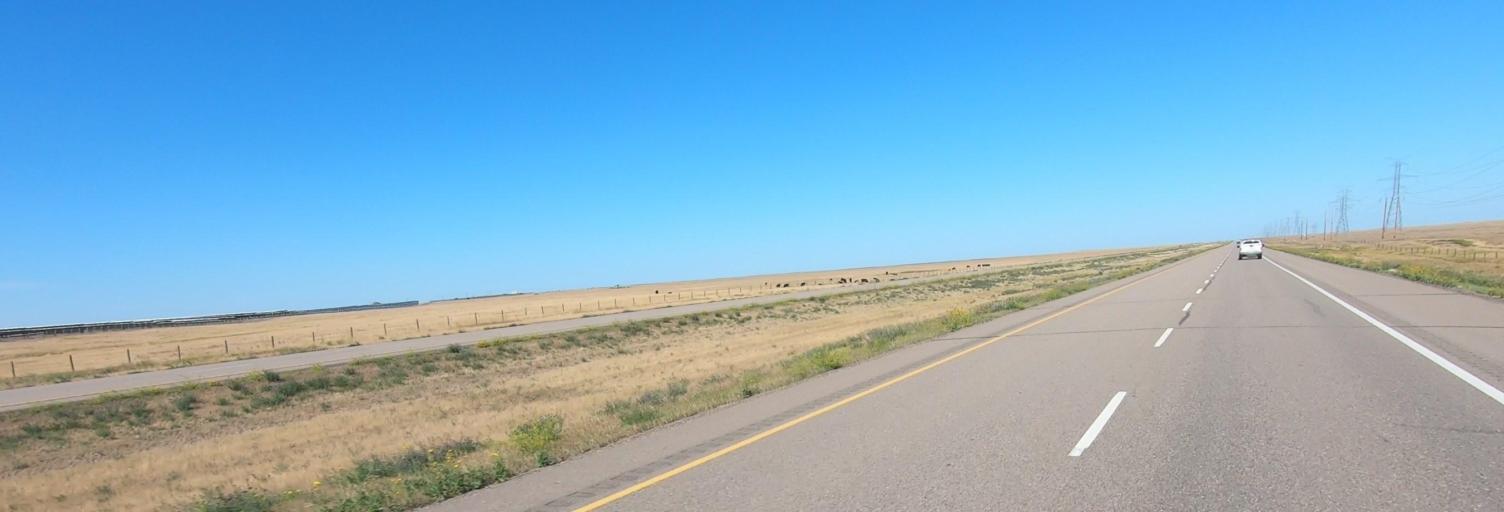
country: CA
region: Alberta
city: Bow Island
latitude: 50.2749
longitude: -111.2717
